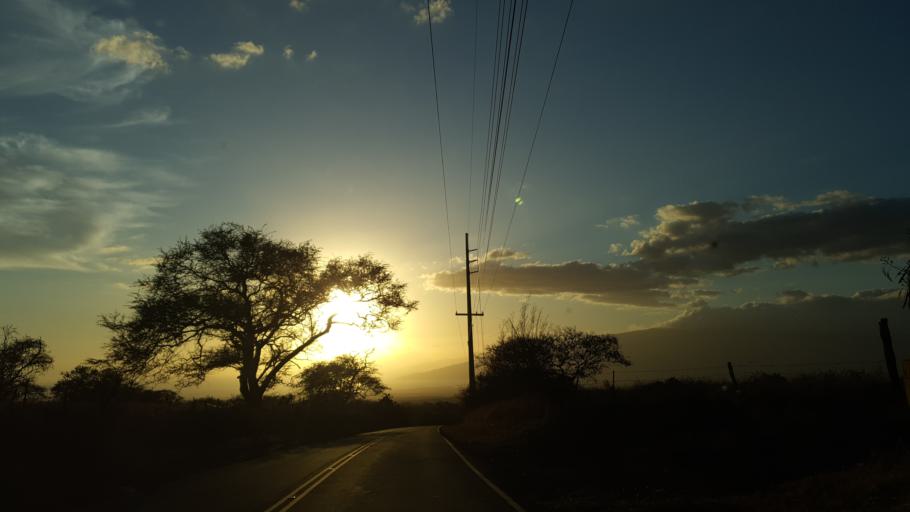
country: US
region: Hawaii
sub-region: Maui County
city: Pukalani
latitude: 20.7927
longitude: -156.3608
